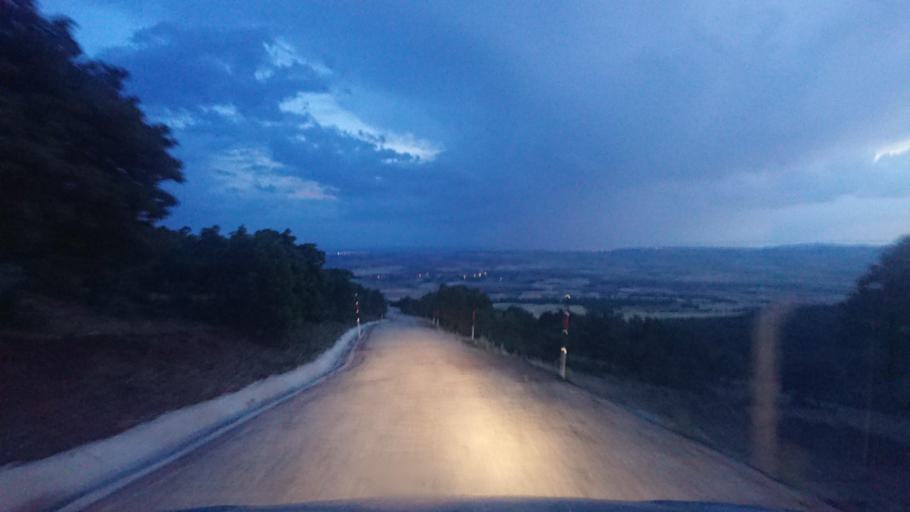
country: TR
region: Aksaray
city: Ortakoy
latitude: 38.6431
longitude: 34.0222
